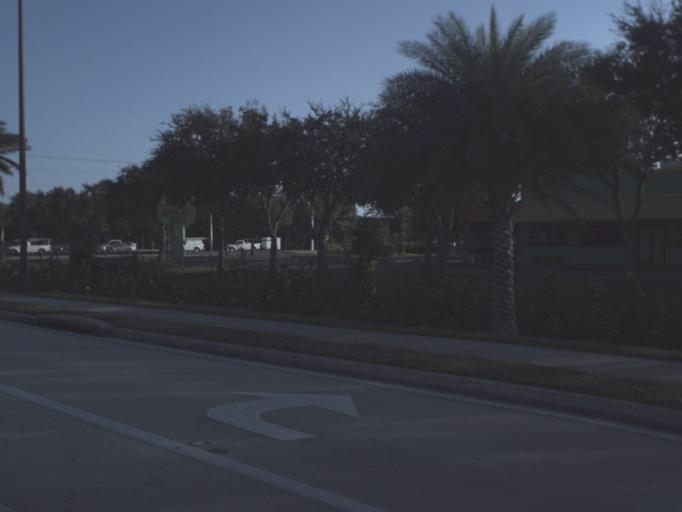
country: US
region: Florida
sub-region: Lee County
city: Bonita Springs
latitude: 26.3295
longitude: -81.8057
